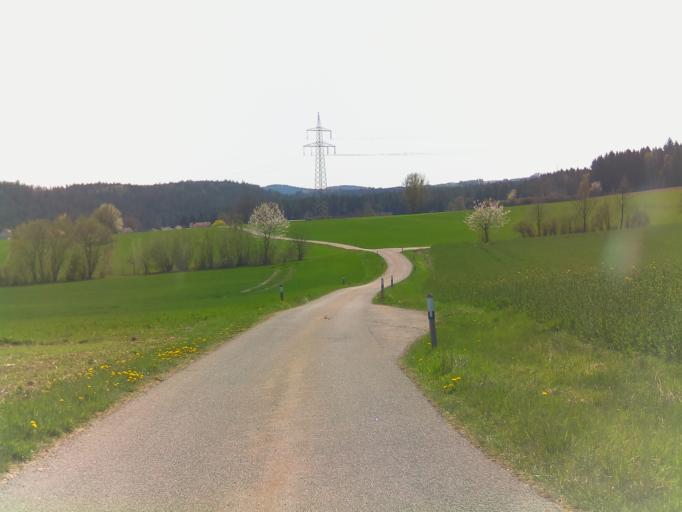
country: DE
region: Bavaria
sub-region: Upper Palatinate
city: Kastl
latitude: 49.4049
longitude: 11.6650
